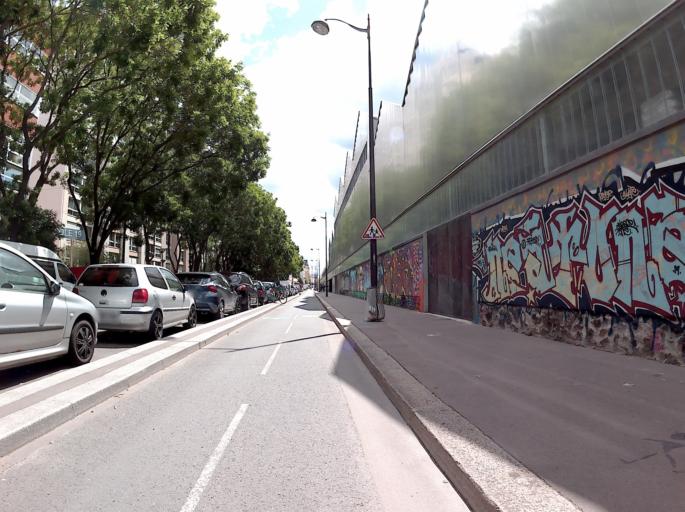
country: FR
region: Ile-de-France
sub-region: Departement de Seine-Saint-Denis
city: Aubervilliers
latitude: 48.8926
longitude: 2.3694
